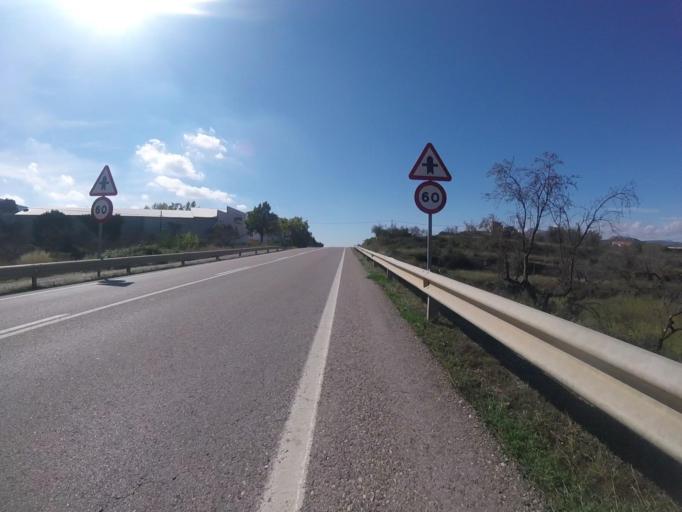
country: ES
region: Valencia
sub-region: Provincia de Castello
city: Albocasser
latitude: 40.3364
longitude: -0.0118
